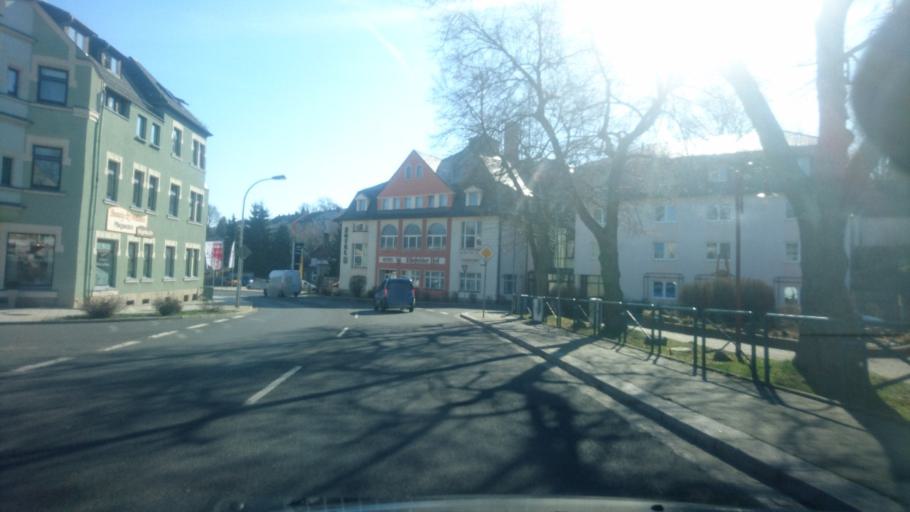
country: DE
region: Saxony
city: Ellefeld
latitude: 50.4825
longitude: 12.3849
